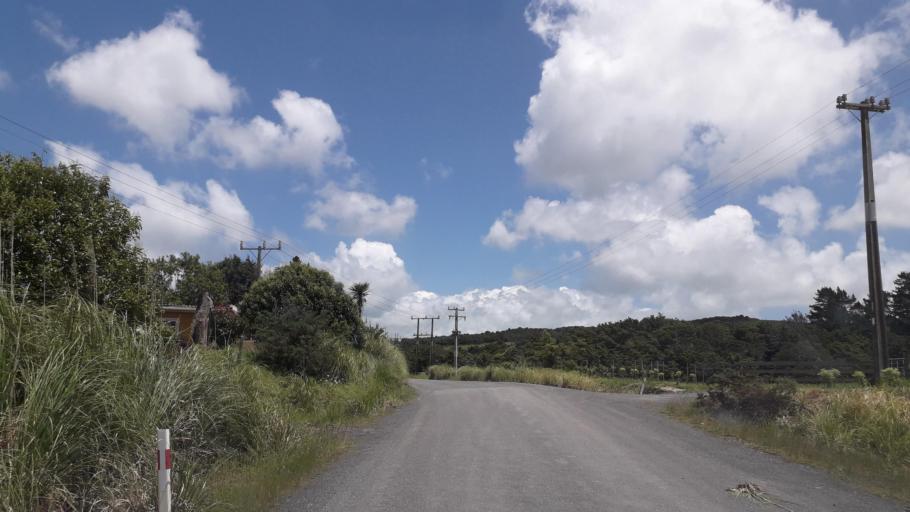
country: NZ
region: Northland
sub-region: Far North District
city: Taipa
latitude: -35.0137
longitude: 173.4194
